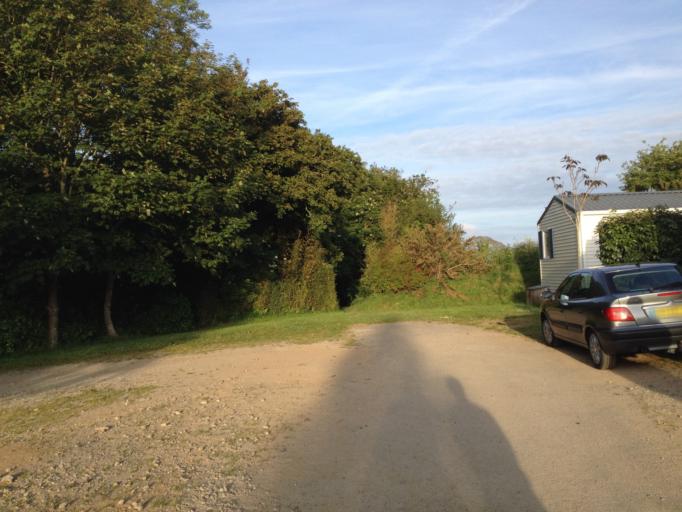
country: FR
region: Brittany
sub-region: Departement du Finistere
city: Roscanvel
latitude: 48.3647
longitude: -4.5367
